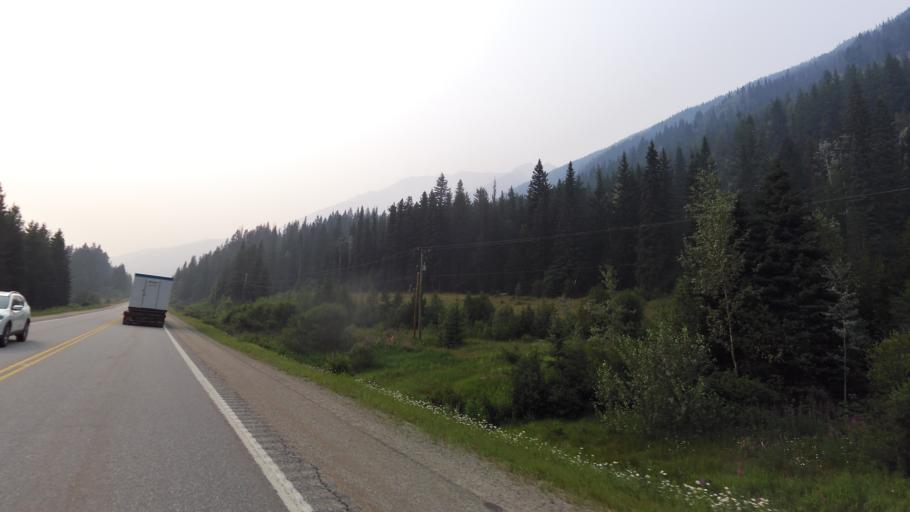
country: CA
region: Alberta
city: Grande Cache
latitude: 53.0136
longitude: -119.0734
